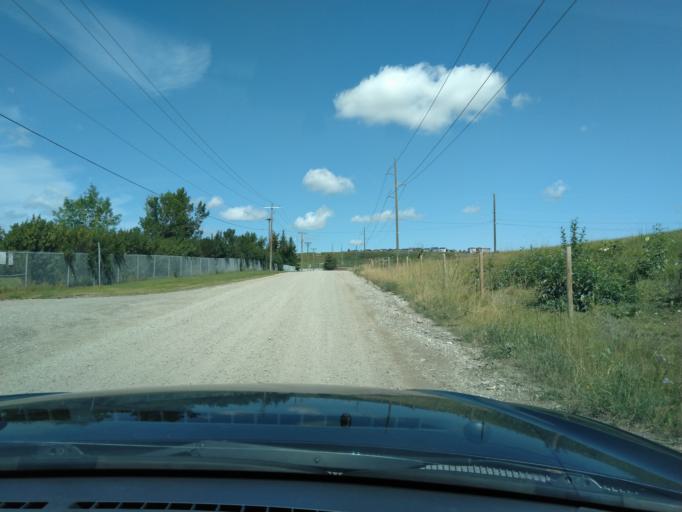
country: CA
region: Alberta
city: Calgary
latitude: 51.1005
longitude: -114.2343
